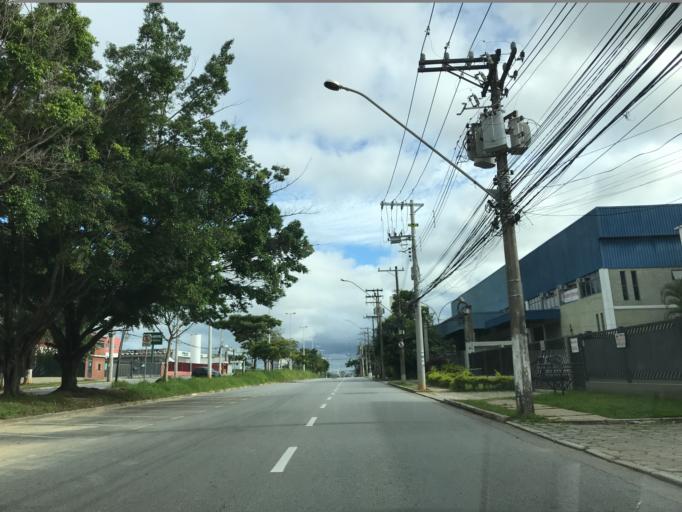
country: BR
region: Sao Paulo
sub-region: Carapicuiba
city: Carapicuiba
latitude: -23.4929
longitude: -46.8353
